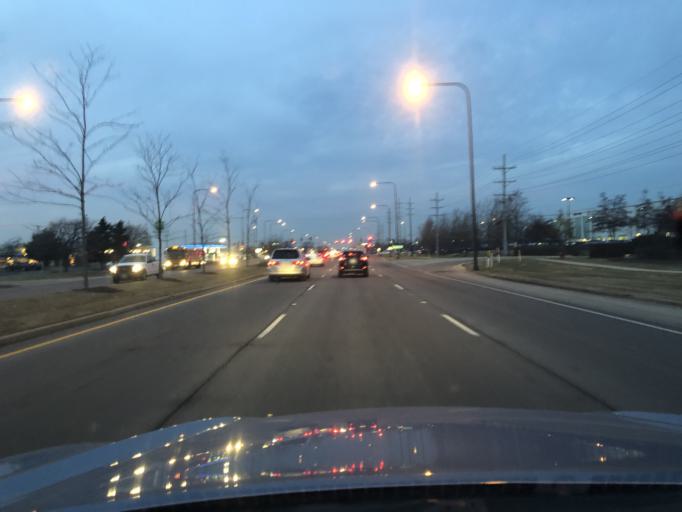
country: US
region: Illinois
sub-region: Cook County
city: Elk Grove Village
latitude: 42.0092
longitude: -87.9596
